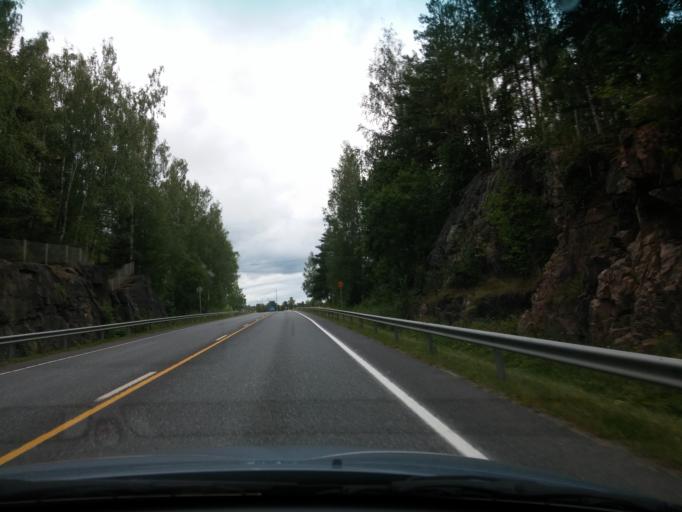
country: FI
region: Uusimaa
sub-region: Porvoo
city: Askola
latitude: 60.4915
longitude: 25.5561
